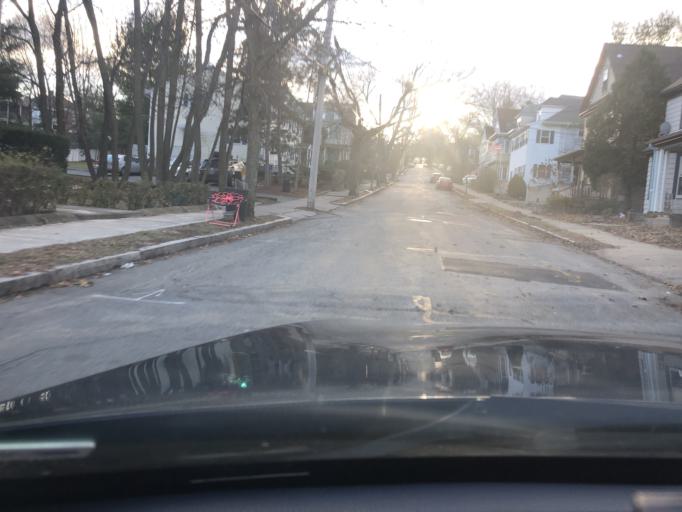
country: US
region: Massachusetts
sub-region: Middlesex County
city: Arlington
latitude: 42.4187
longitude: -71.1677
